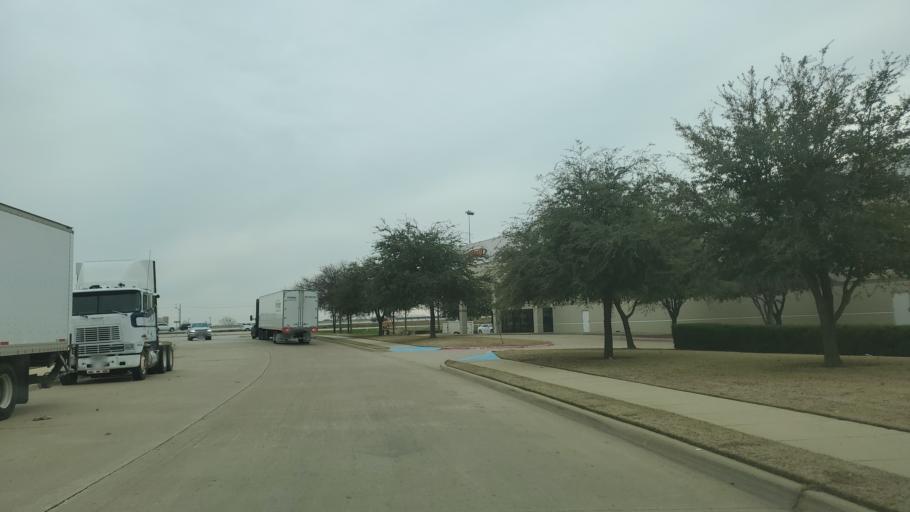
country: US
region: Texas
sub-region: Dallas County
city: Coppell
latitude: 32.9847
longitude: -97.0188
